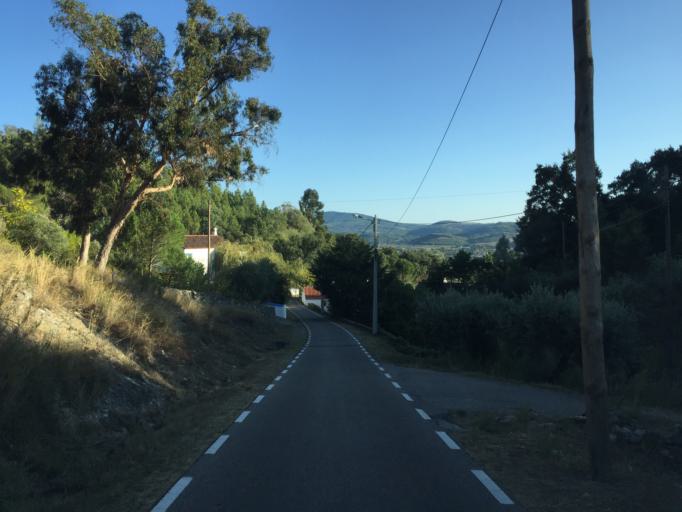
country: PT
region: Portalegre
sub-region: Marvao
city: Marvao
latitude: 39.3975
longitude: -7.3896
